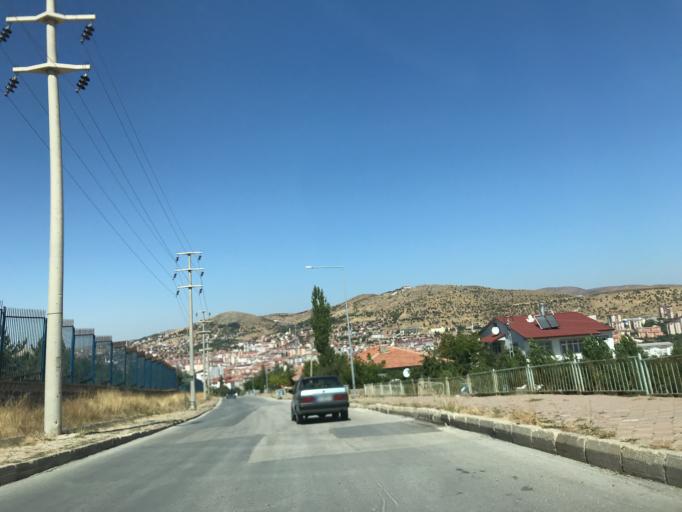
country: TR
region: Yozgat
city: Yozgat
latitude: 39.8155
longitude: 34.8224
